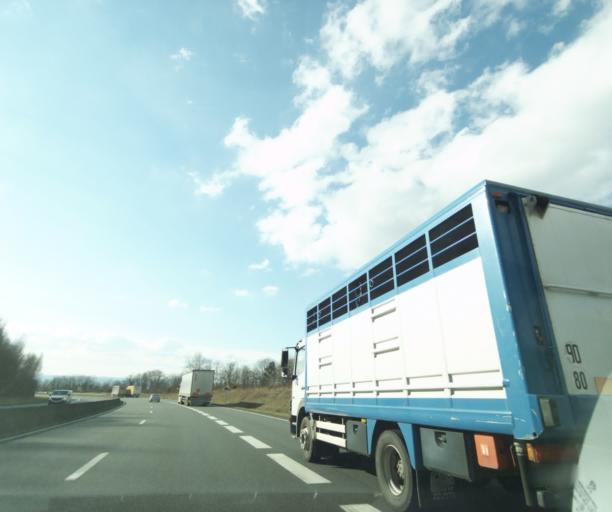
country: FR
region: Limousin
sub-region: Departement de la Correze
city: Donzenac
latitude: 45.2466
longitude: 1.5177
